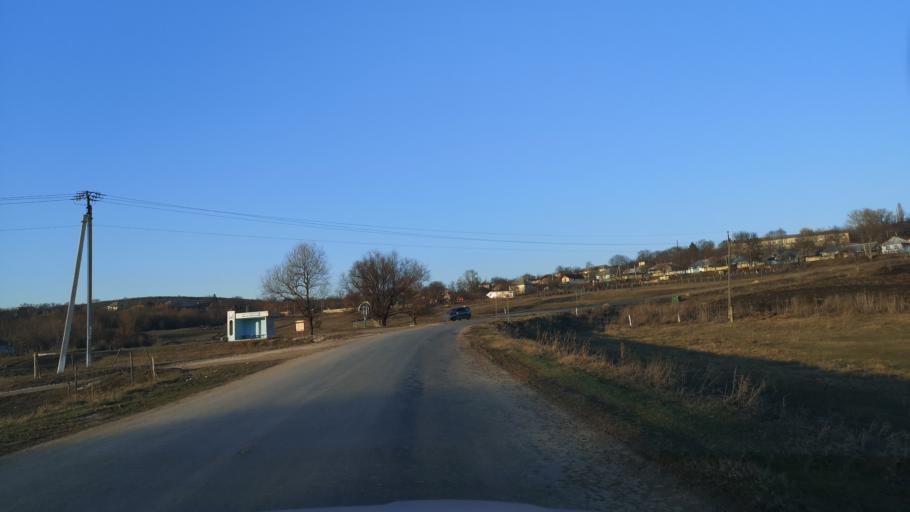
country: MD
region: Orhei
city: Orhei
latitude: 47.3534
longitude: 28.6947
